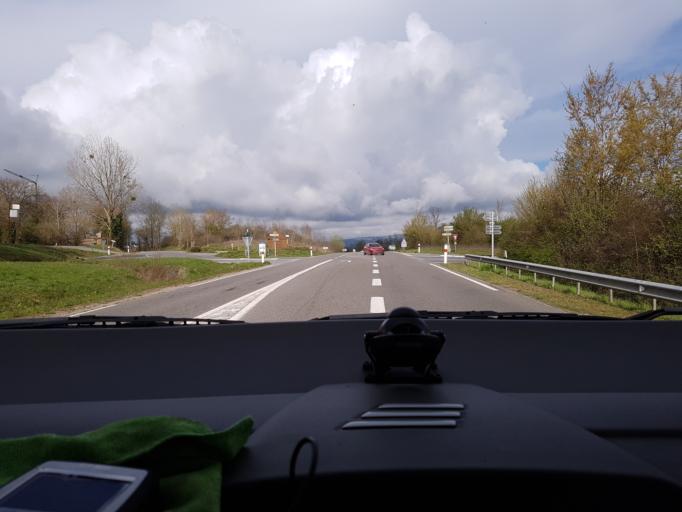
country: FR
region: Midi-Pyrenees
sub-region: Departement de l'Aveyron
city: Moyrazes
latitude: 44.3800
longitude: 2.4528
